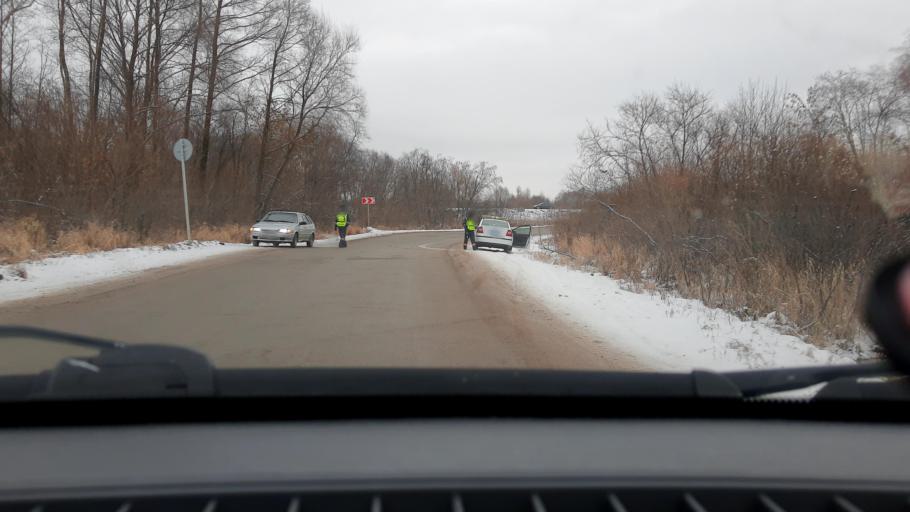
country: RU
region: Bashkortostan
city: Iglino
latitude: 54.8394
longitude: 56.4503
